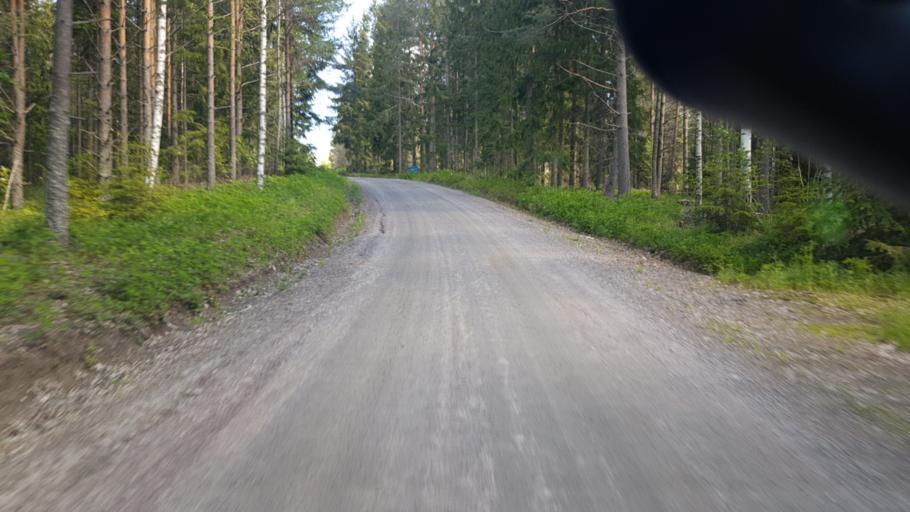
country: SE
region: Vaermland
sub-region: Grums Kommun
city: Slottsbron
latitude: 59.4642
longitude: 12.9195
